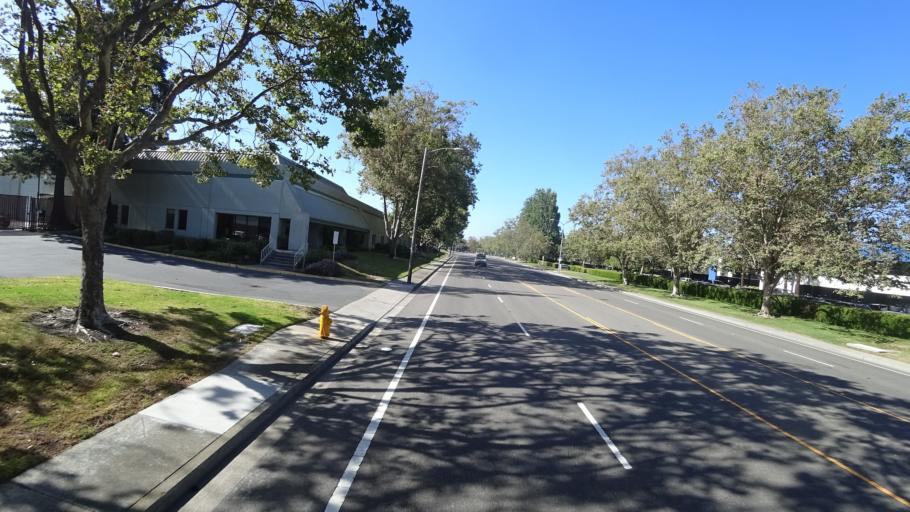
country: US
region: California
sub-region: Alameda County
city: Union City
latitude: 37.6092
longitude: -122.0548
